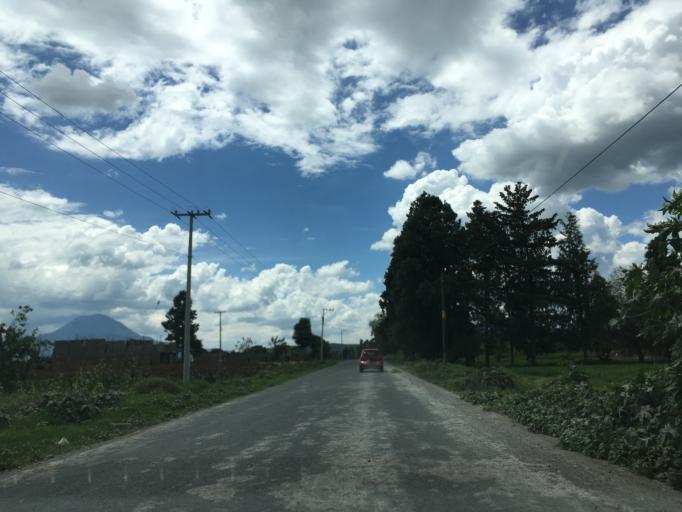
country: MX
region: Michoacan
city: Zacapu
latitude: 19.8399
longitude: -101.7548
